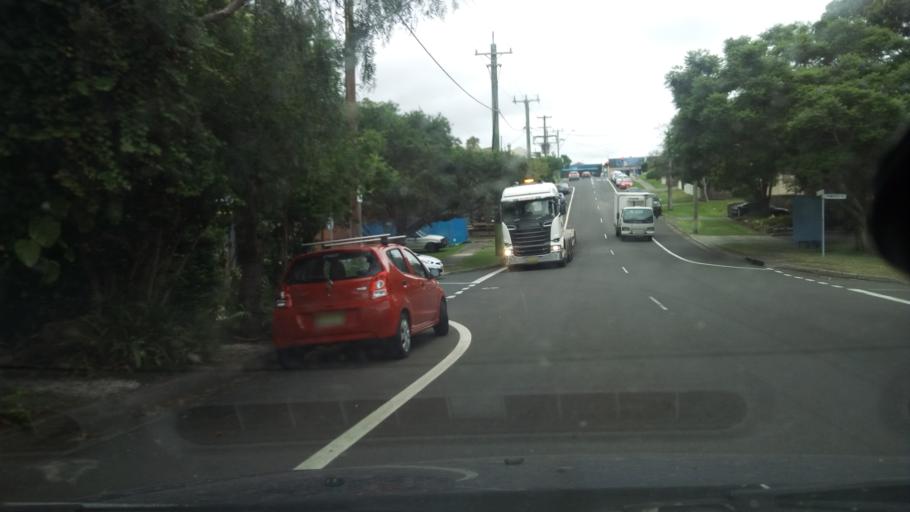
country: AU
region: New South Wales
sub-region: Wollongong
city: Mangerton
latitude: -34.4275
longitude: 150.8774
